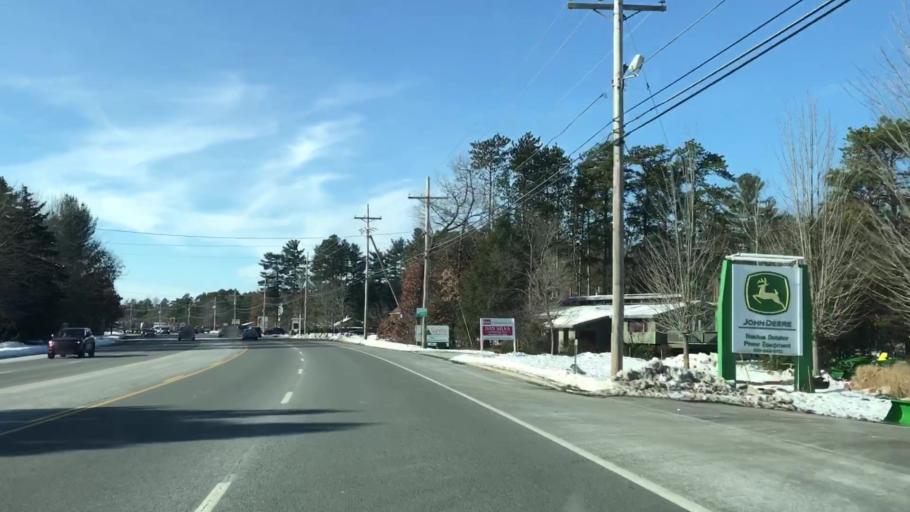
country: US
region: New Hampshire
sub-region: Hillsborough County
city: Hollis
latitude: 42.8106
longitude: -71.5758
